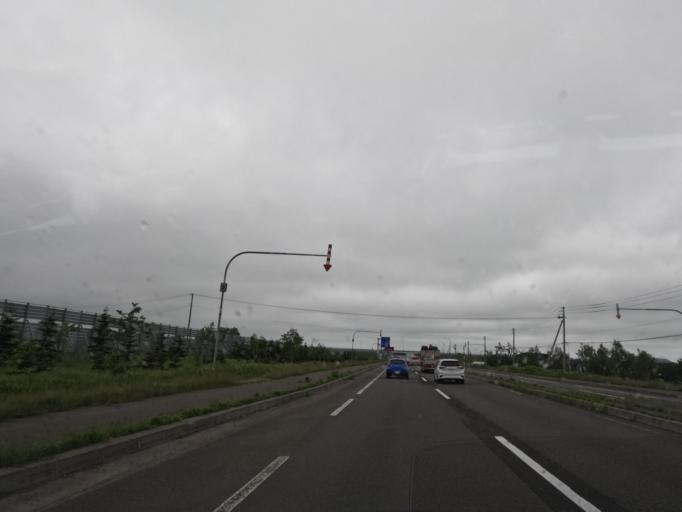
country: JP
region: Hokkaido
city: Tobetsu
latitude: 43.1797
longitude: 141.5227
